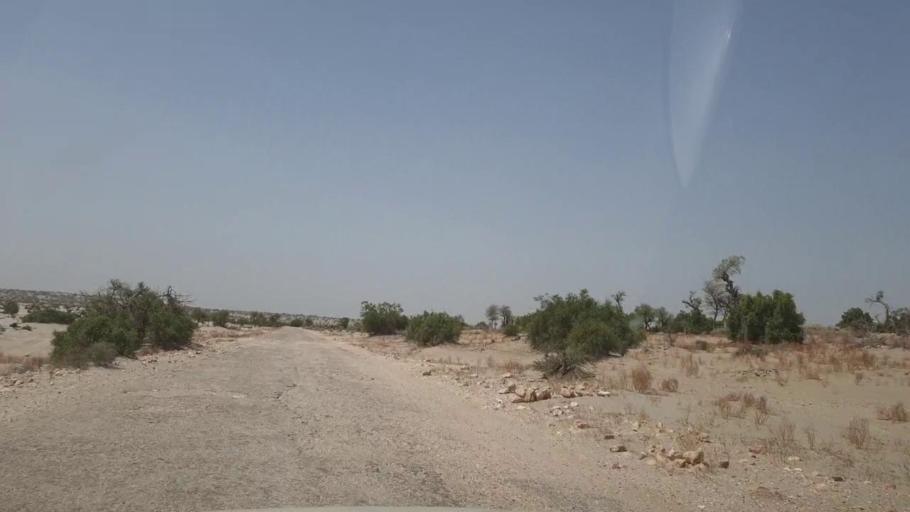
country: PK
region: Sindh
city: Khanpur
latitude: 27.3420
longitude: 69.3165
